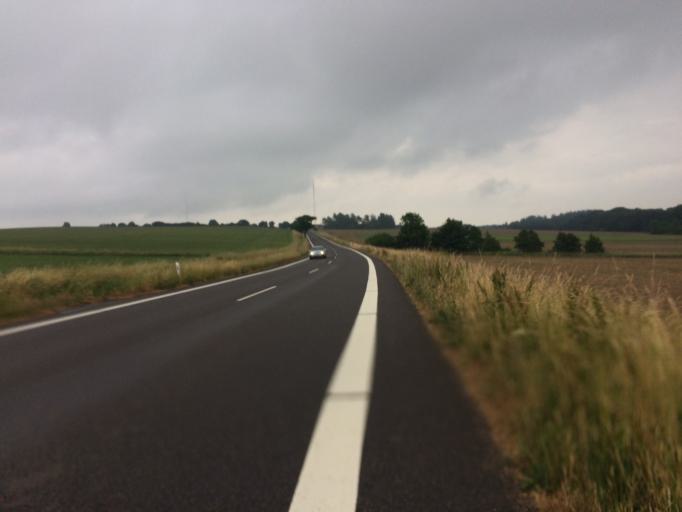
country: DK
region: Capital Region
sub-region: Bornholm Kommune
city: Akirkeby
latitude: 55.1399
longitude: 14.8595
